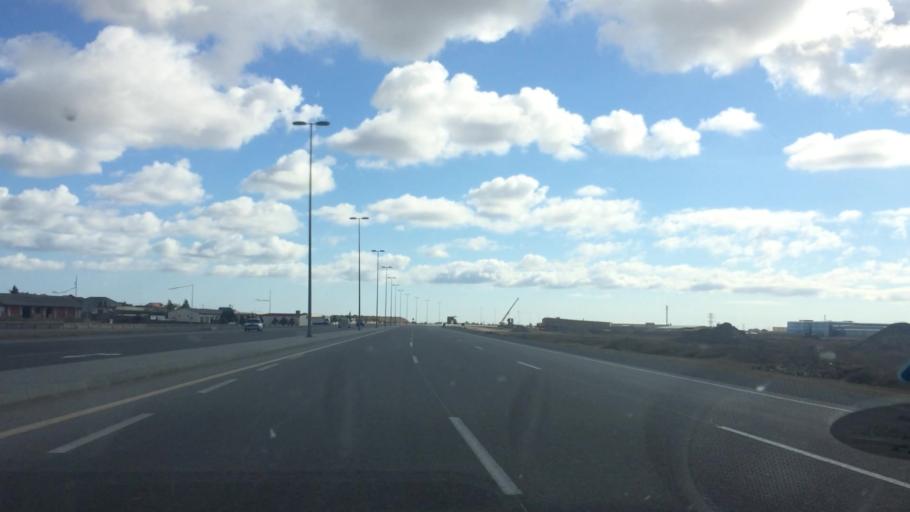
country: AZ
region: Baki
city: Qala
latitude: 40.4565
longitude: 50.1366
